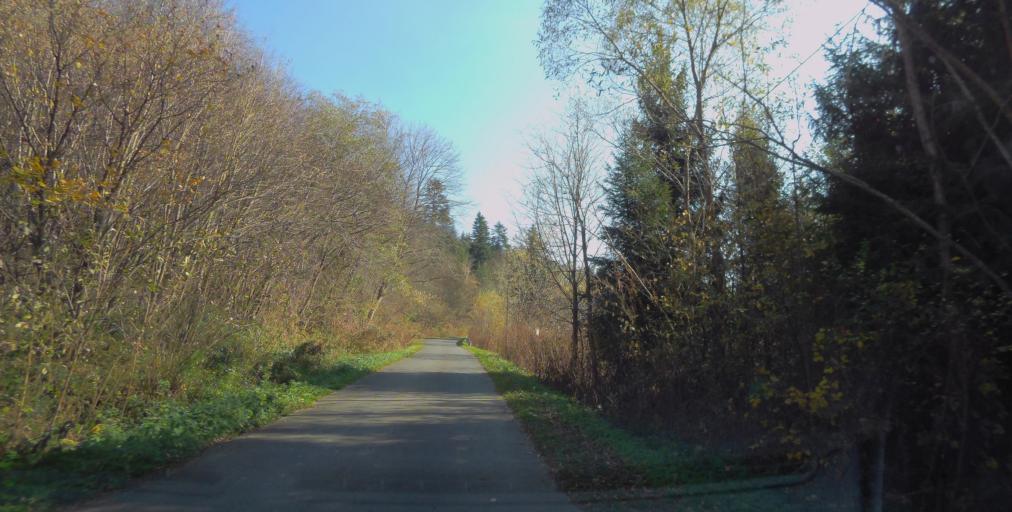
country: PL
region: Subcarpathian Voivodeship
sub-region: Powiat leski
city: Polanczyk
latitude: 49.3263
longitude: 22.4293
